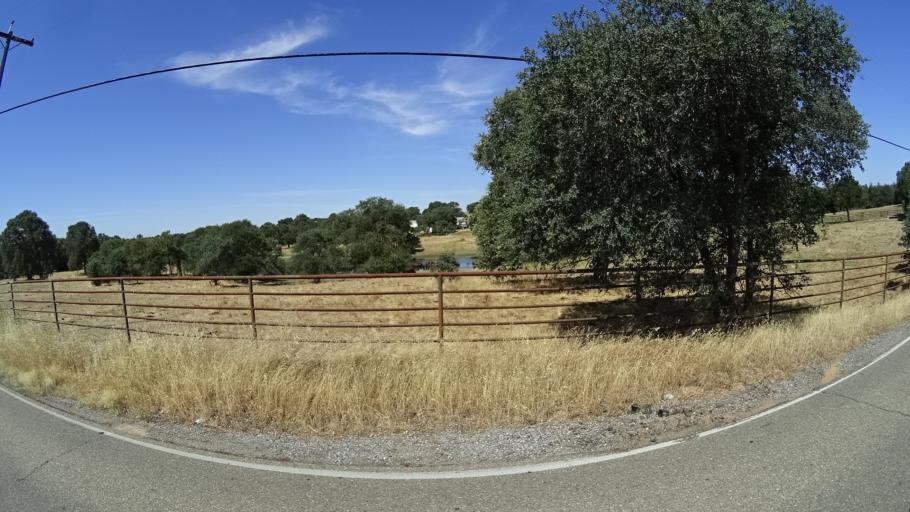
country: US
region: California
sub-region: Calaveras County
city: Rancho Calaveras
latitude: 38.1444
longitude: -120.8992
